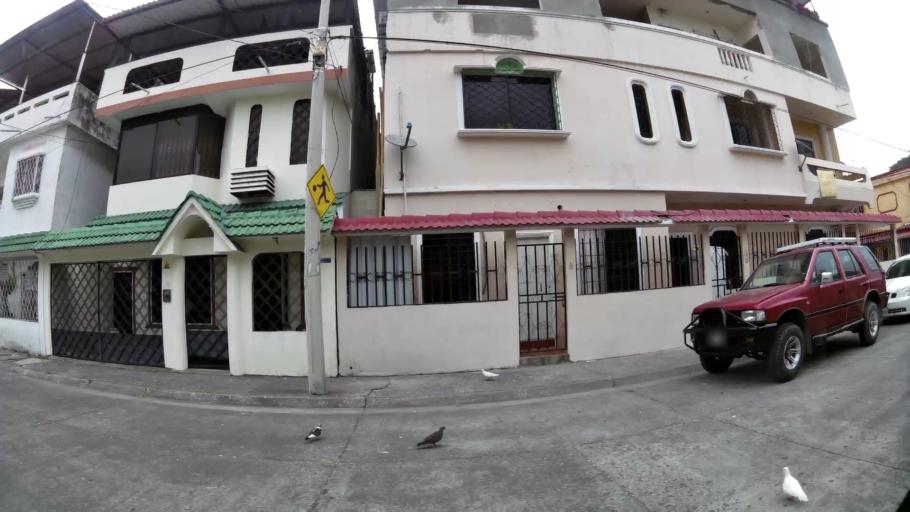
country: EC
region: Guayas
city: Eloy Alfaro
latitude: -2.1423
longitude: -79.8853
